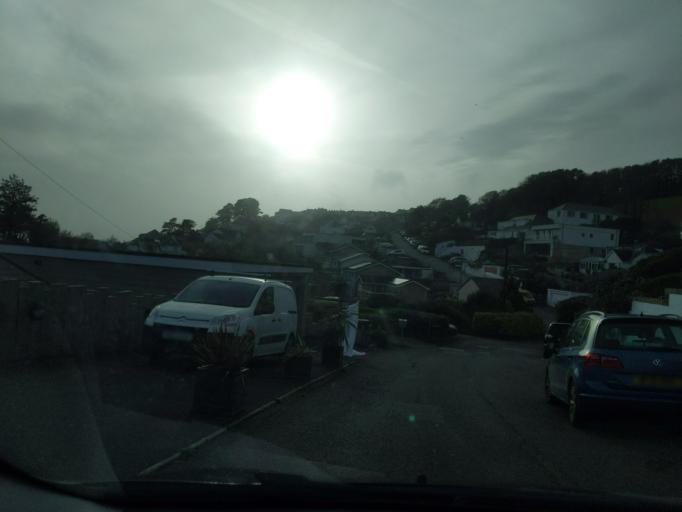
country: GB
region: England
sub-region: Cornwall
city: Looe
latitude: 50.3598
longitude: -4.4413
